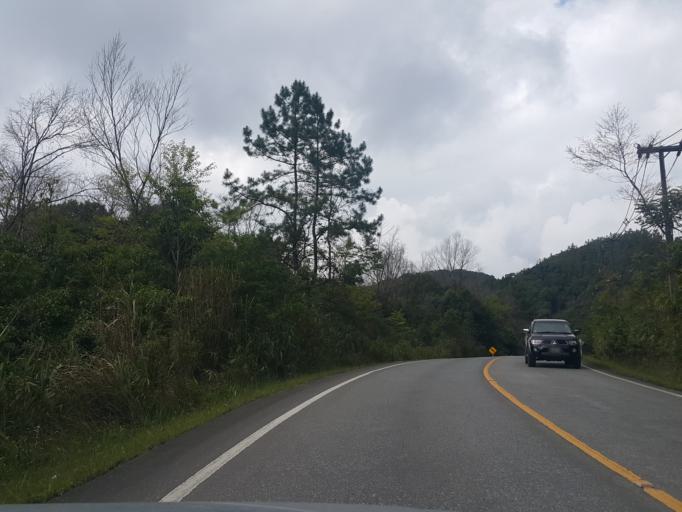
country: TH
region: Chiang Mai
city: Mae Chaem
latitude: 18.5089
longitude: 98.5099
